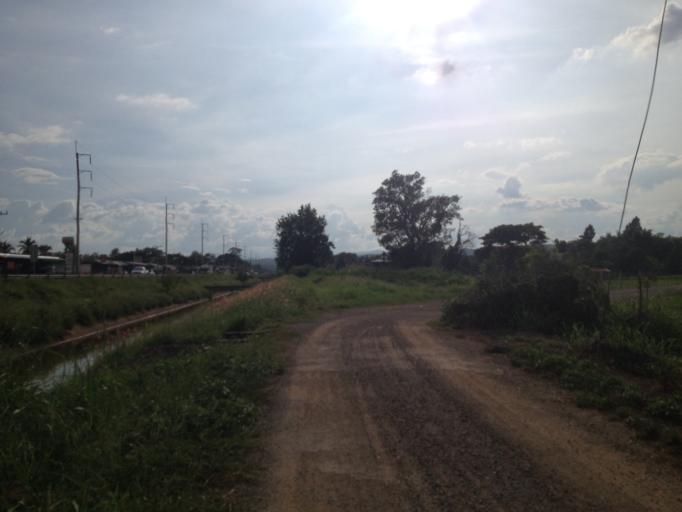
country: TH
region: Chiang Mai
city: Hang Dong
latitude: 18.7087
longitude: 98.9179
